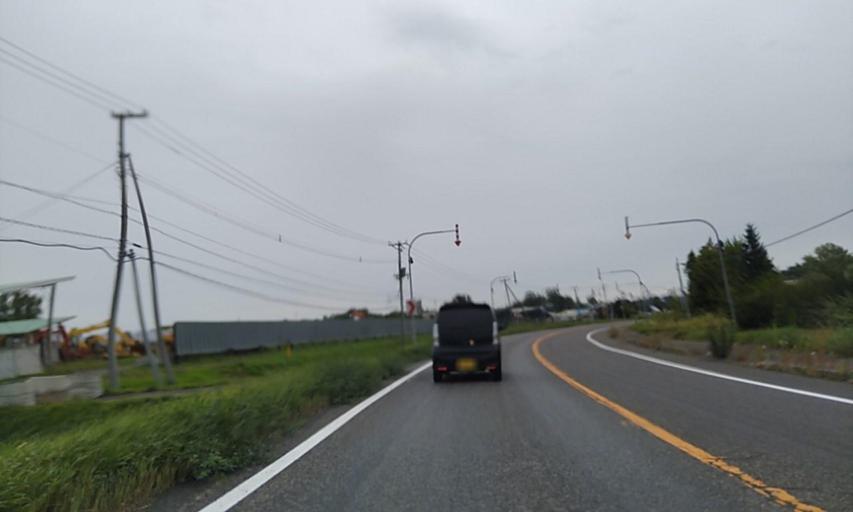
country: JP
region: Hokkaido
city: Bihoro
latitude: 43.9161
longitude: 144.1609
